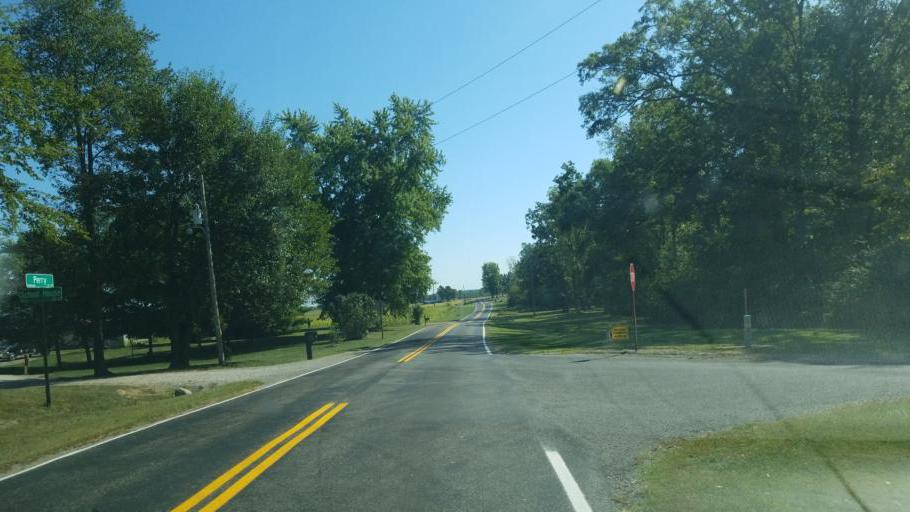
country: US
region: Ohio
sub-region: Champaign County
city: North Lewisburg
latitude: 40.1475
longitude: -83.6015
